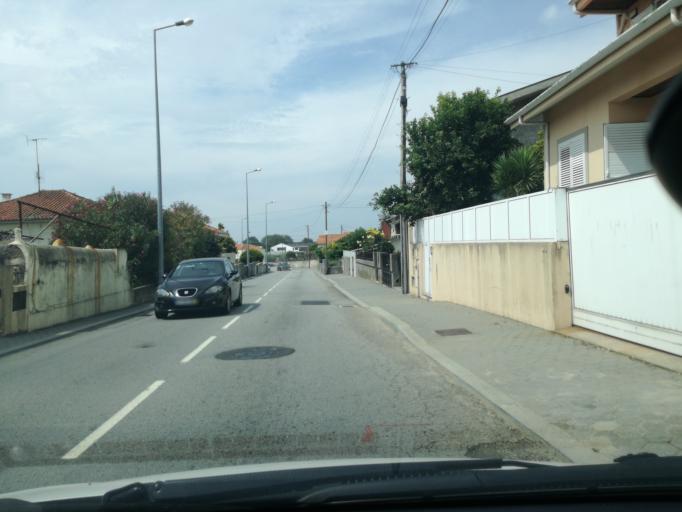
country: PT
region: Porto
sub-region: Vila Nova de Gaia
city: Grijo
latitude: 41.0429
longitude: -8.5748
